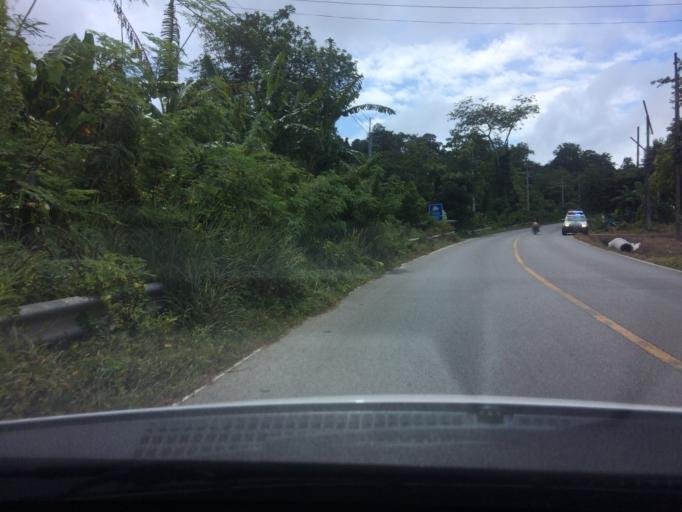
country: TH
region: Phuket
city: Thalang
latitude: 8.0857
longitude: 98.3663
